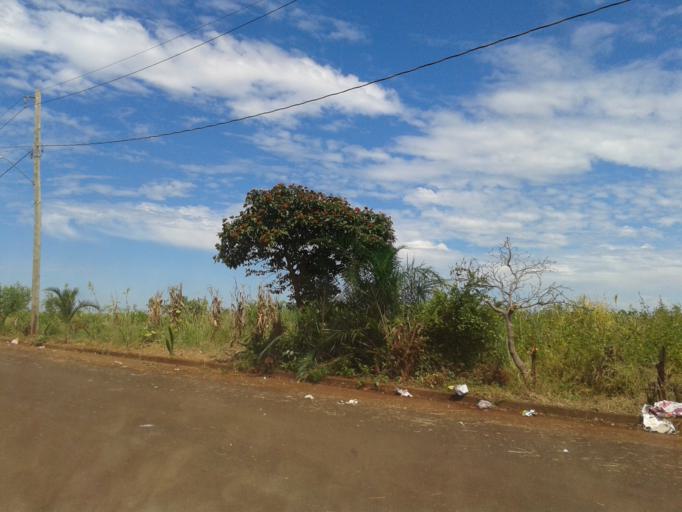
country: BR
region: Minas Gerais
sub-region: Capinopolis
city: Capinopolis
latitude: -18.5219
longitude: -49.5038
